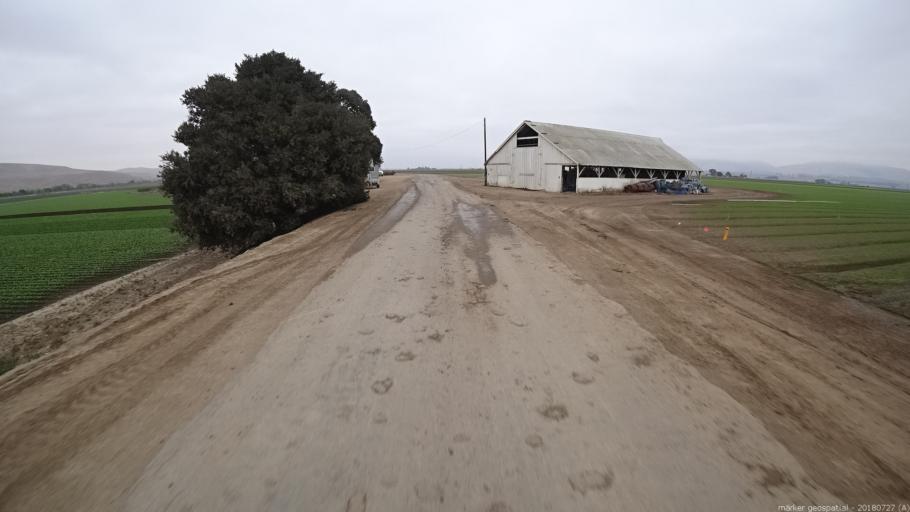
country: US
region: California
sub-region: Monterey County
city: Greenfield
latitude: 36.3262
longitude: -121.2063
